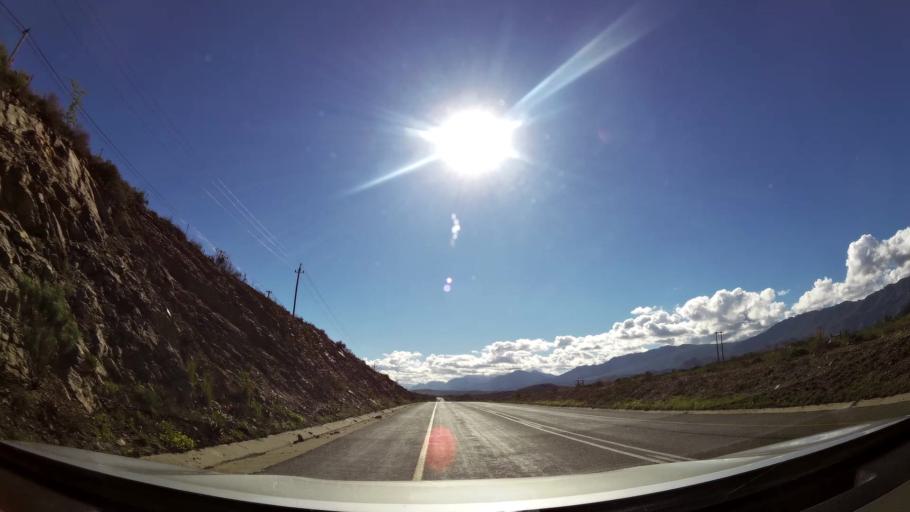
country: ZA
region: Western Cape
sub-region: Cape Winelands District Municipality
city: Ashton
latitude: -33.7858
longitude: 19.7717
